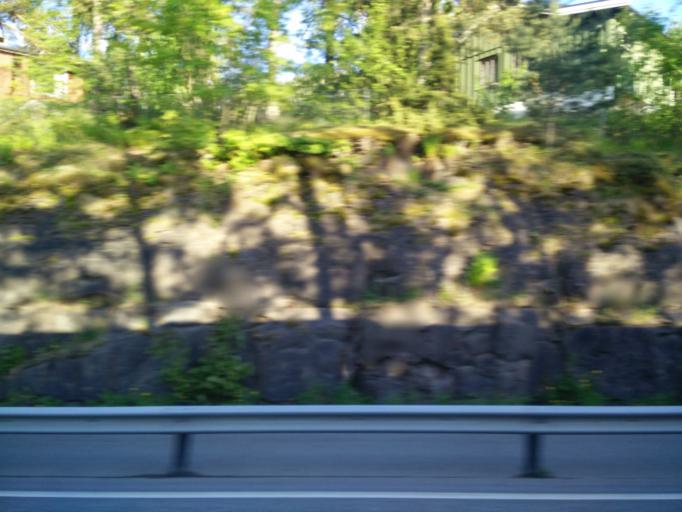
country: NO
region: Buskerud
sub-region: Hole
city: Vik
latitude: 60.0571
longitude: 10.2971
